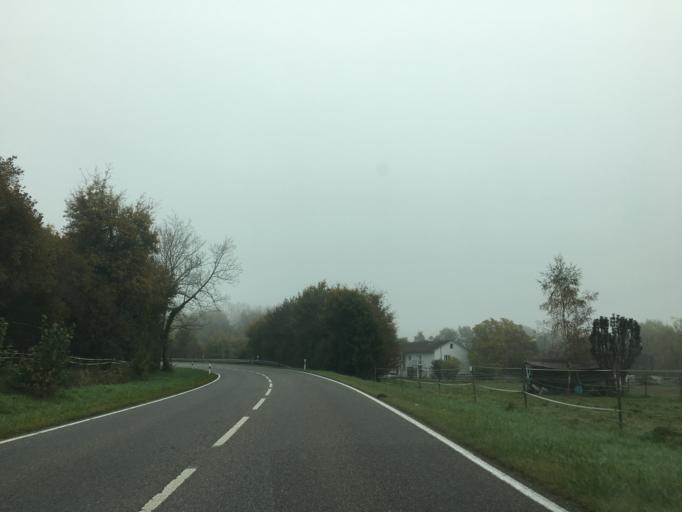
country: CH
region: Thurgau
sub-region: Kreuzlingen District
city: Gottlieben
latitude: 47.7002
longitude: 9.1551
